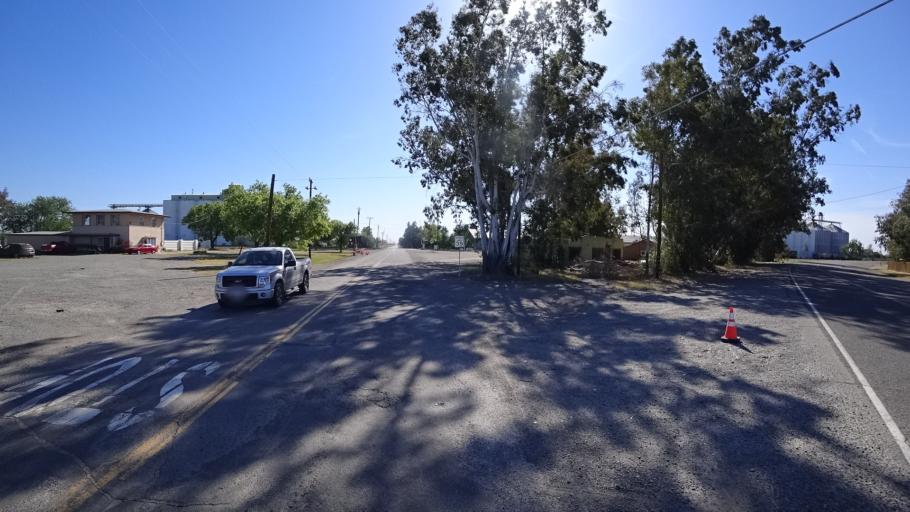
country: US
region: California
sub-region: Glenn County
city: Willows
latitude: 39.6241
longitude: -122.1953
